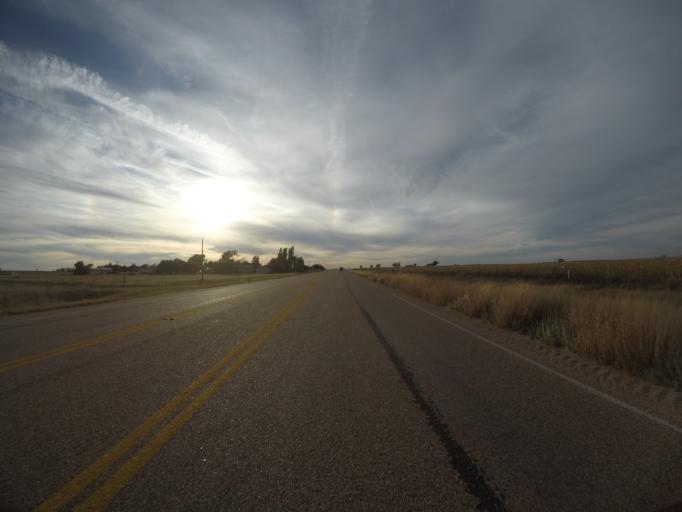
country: US
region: Colorado
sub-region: Yuma County
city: Yuma
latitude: 39.6561
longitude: -102.6210
